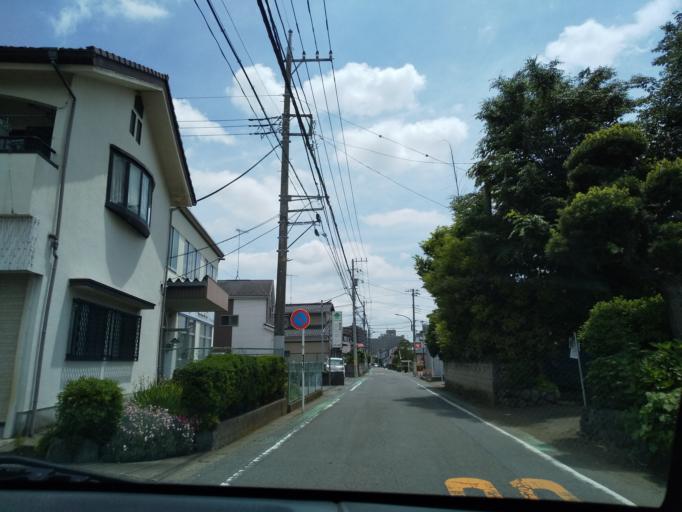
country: JP
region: Kanagawa
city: Zama
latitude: 35.5617
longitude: 139.3544
